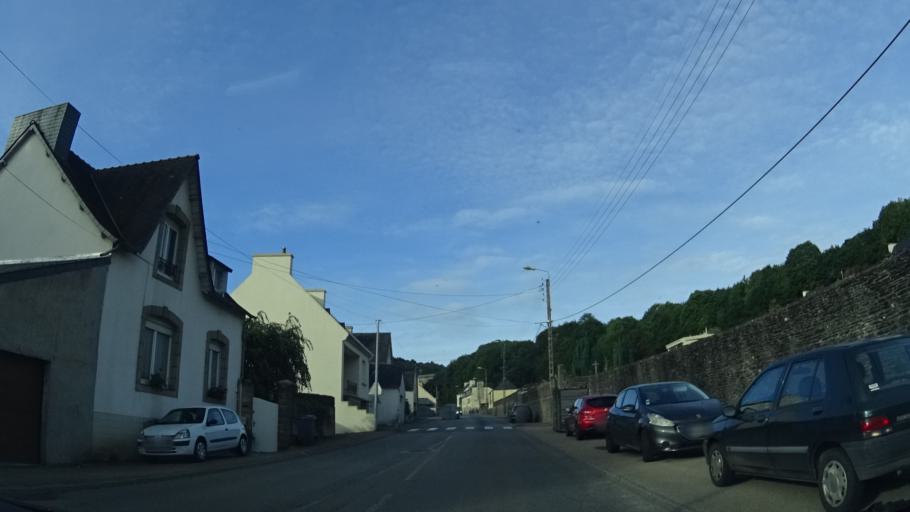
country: FR
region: Brittany
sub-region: Departement du Finistere
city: Chateaulin
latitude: 48.1972
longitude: -4.0989
